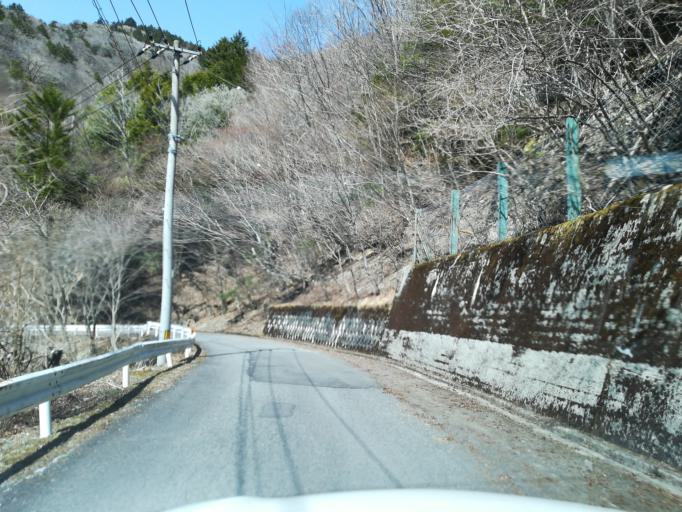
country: JP
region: Tokushima
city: Wakimachi
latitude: 33.8662
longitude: 134.0755
